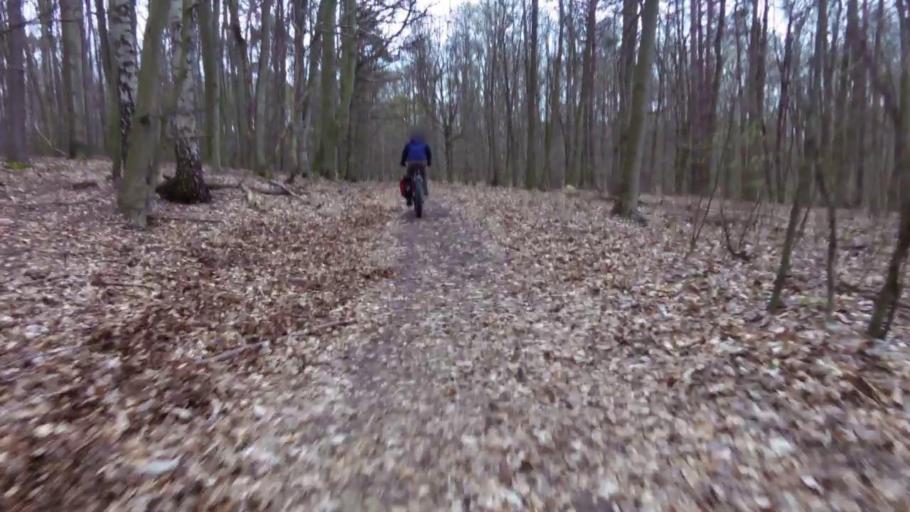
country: PL
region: West Pomeranian Voivodeship
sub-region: Powiat kamienski
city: Wolin
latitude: 53.9802
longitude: 14.6011
